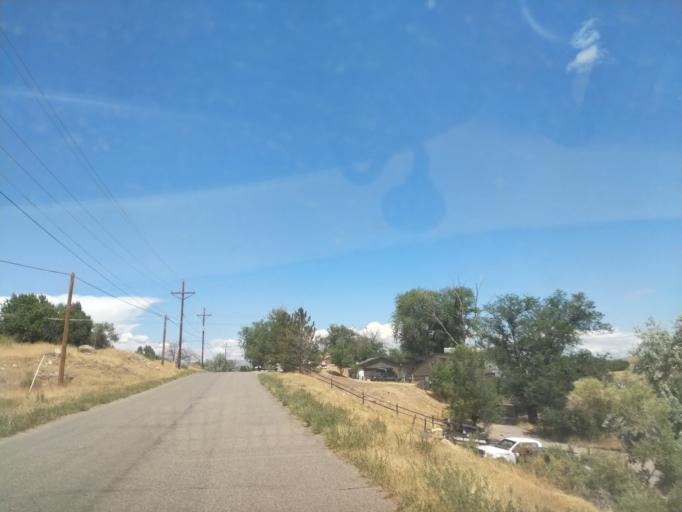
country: US
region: Colorado
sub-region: Mesa County
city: Redlands
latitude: 39.0748
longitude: -108.6397
